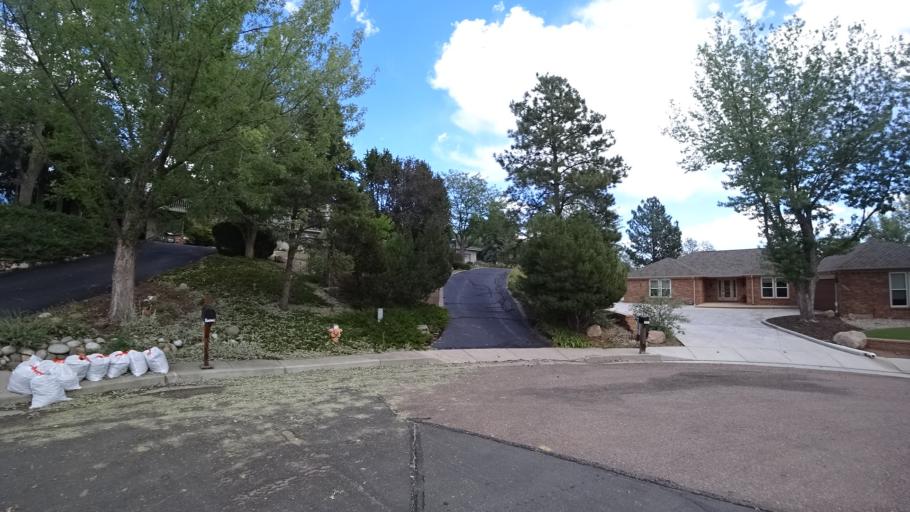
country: US
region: Colorado
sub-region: El Paso County
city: Stratmoor
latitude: 38.7840
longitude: -104.8278
